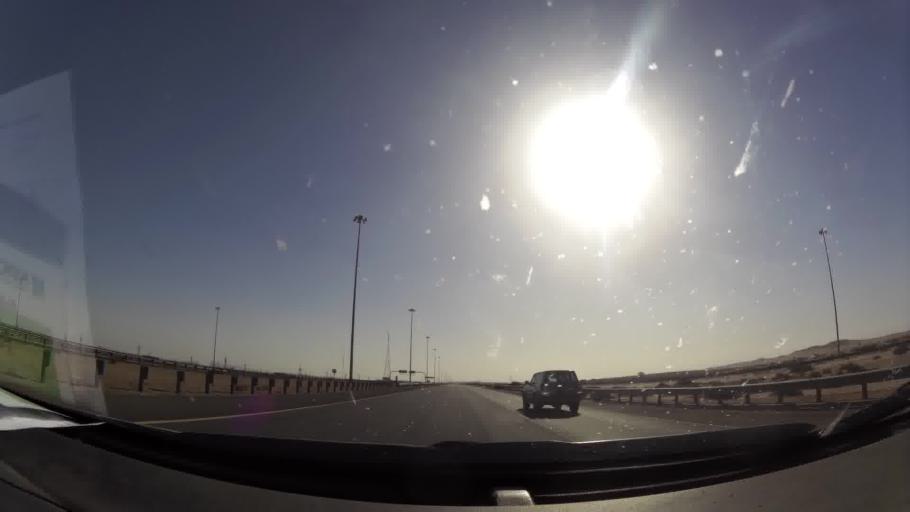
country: KW
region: Al Asimah
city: Kuwait City
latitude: 29.6070
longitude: 47.9138
